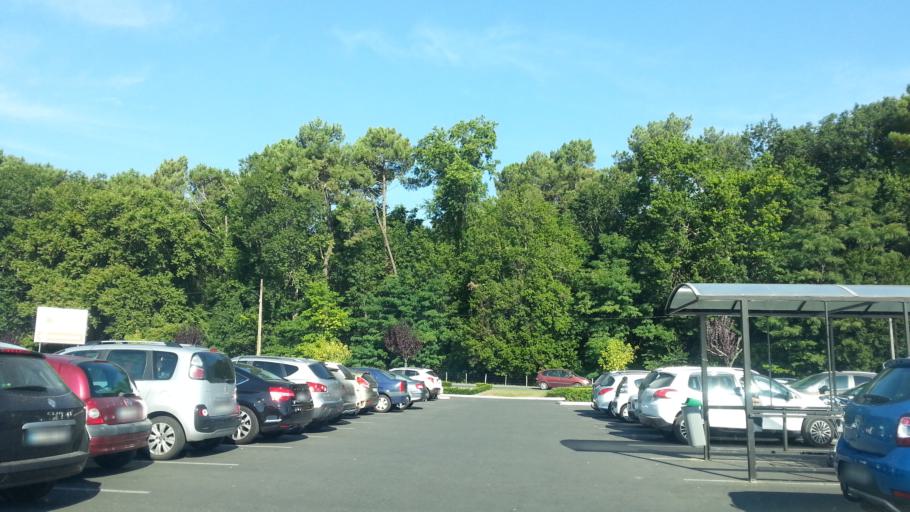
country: FR
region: Aquitaine
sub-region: Departement de la Gironde
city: Leognan
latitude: 44.7469
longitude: -0.5914
